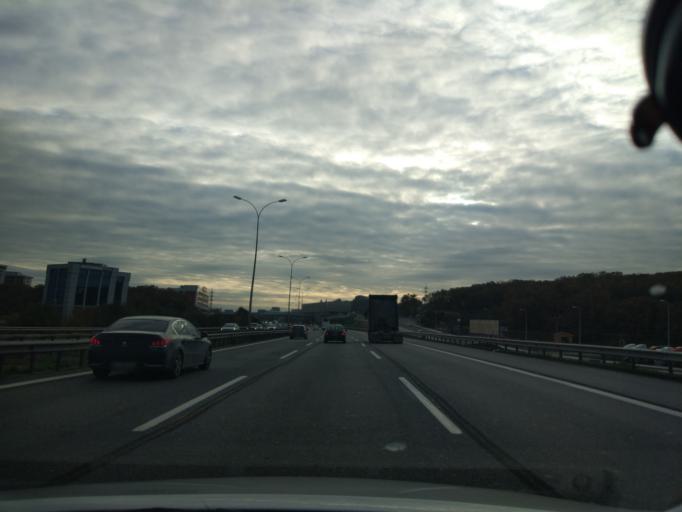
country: TR
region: Istanbul
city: Samandira
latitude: 40.9789
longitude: 29.2213
